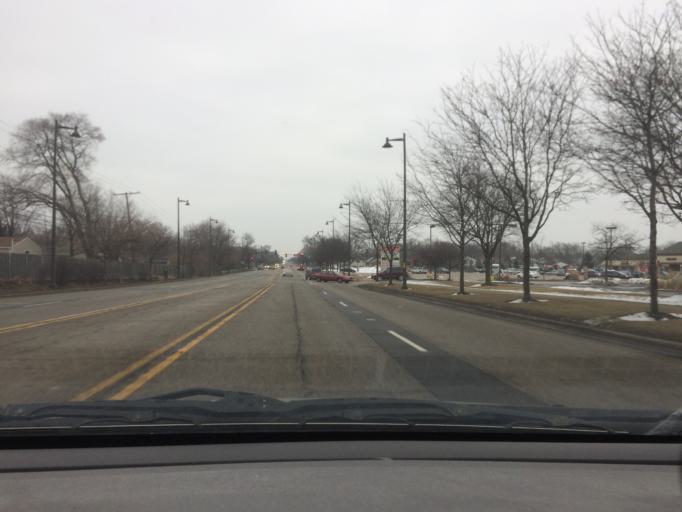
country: US
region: Illinois
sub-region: Cook County
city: Streamwood
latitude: 42.0128
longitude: -88.1789
